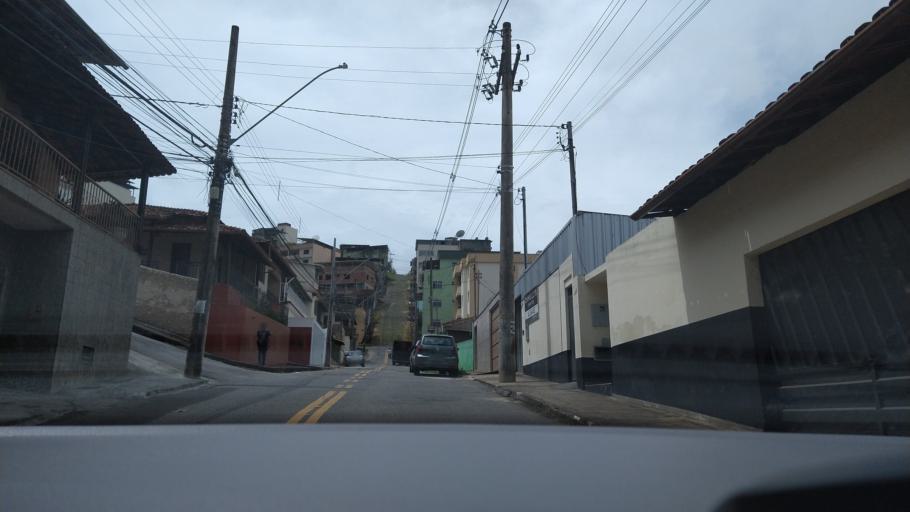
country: BR
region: Minas Gerais
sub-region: Vicosa
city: Vicosa
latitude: -20.7638
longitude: -42.8865
